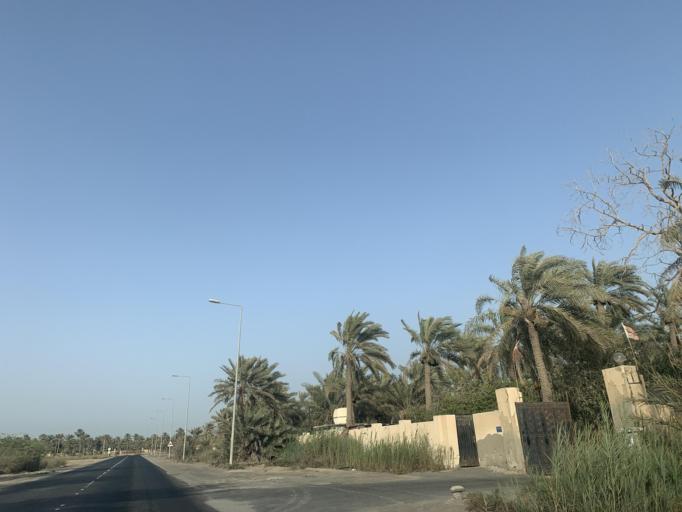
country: BH
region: Central Governorate
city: Madinat Hamad
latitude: 26.1757
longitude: 50.4557
